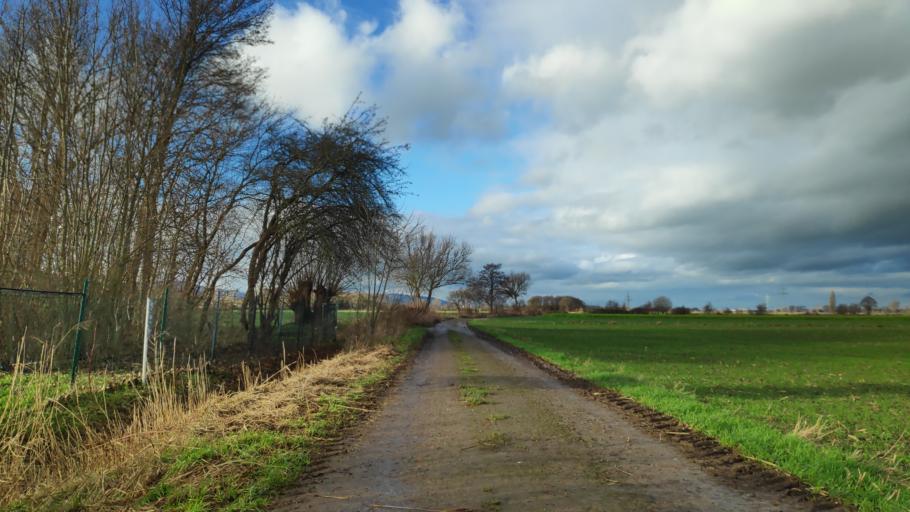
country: DE
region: North Rhine-Westphalia
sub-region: Regierungsbezirk Detmold
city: Minden
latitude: 52.2801
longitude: 8.8466
